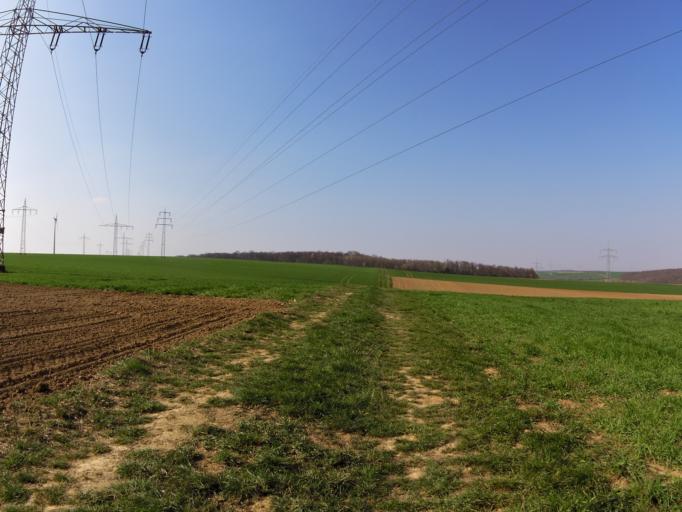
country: DE
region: Bavaria
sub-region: Regierungsbezirk Unterfranken
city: Theilheim
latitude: 49.7681
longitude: 10.0471
